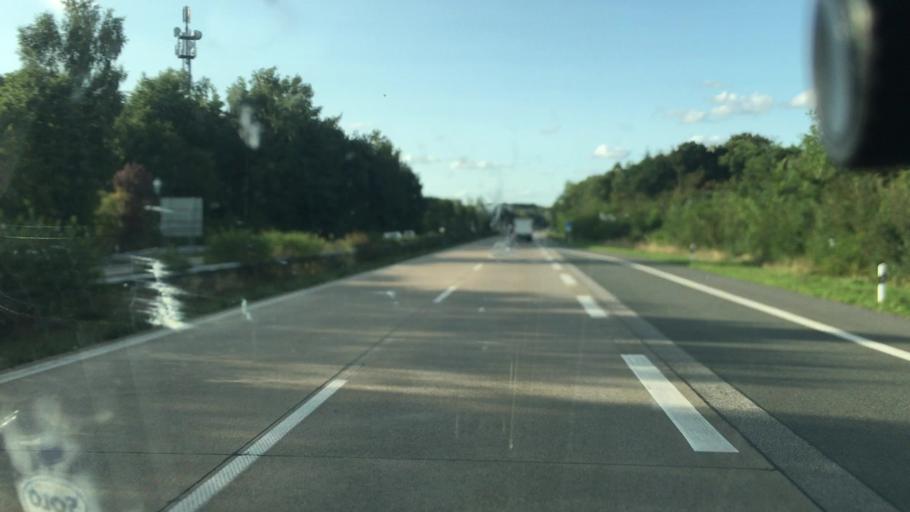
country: DE
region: Lower Saxony
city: Wiefelstede
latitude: 53.2816
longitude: 8.1542
